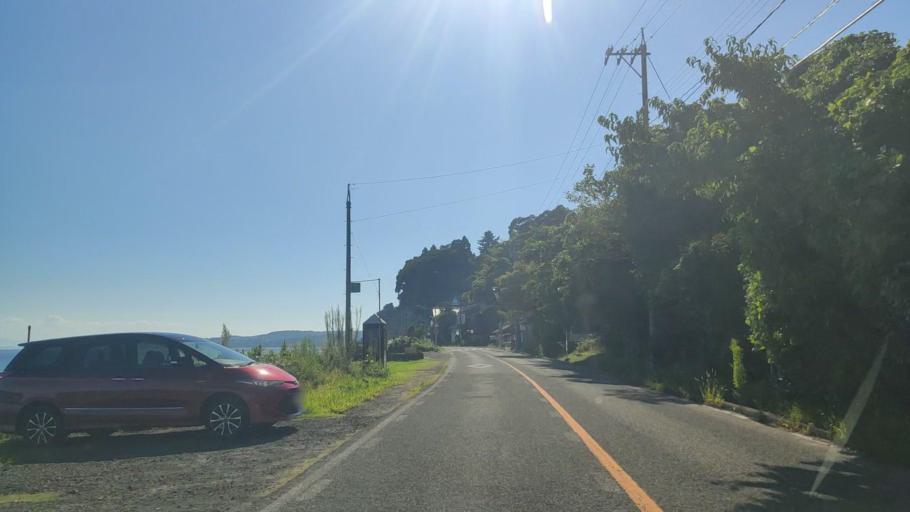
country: JP
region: Ishikawa
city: Nanao
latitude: 37.2853
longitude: 137.1126
